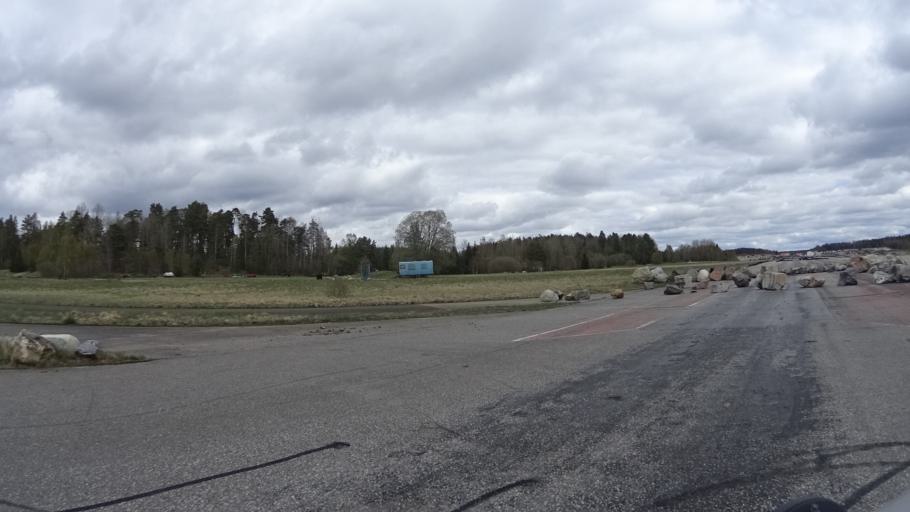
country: SE
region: Stockholm
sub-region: Botkyrka Kommun
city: Tullinge
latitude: 59.1758
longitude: 17.8929
